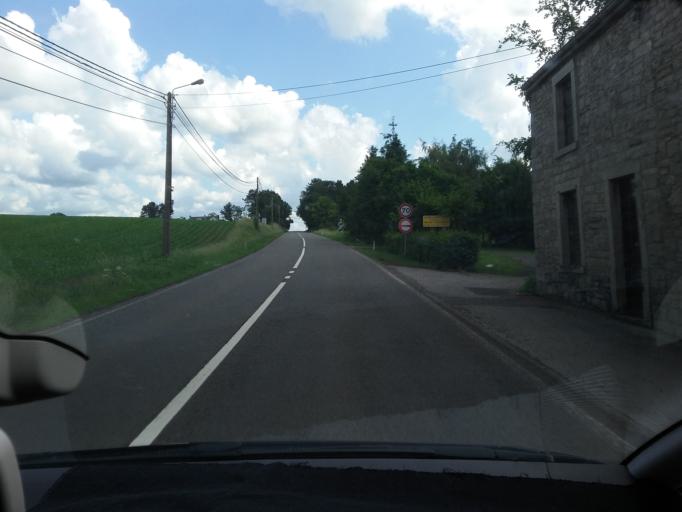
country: BE
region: Wallonia
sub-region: Province de Namur
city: Rochefort
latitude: 50.1399
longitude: 5.2227
